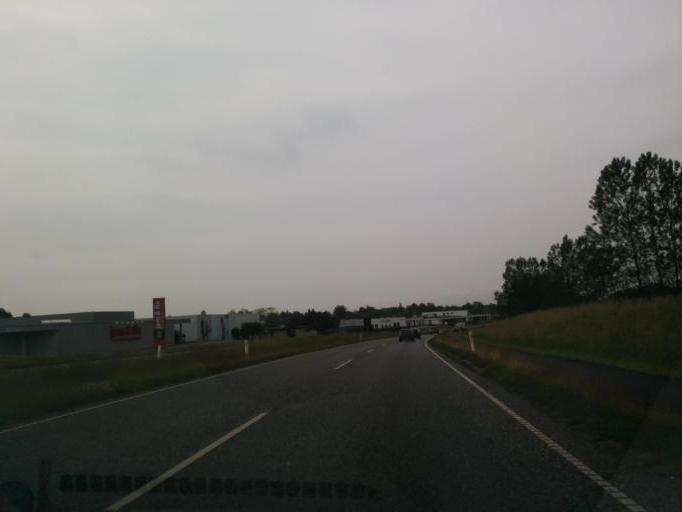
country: DK
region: Central Jutland
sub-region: Arhus Kommune
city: Hjortshoj
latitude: 56.2117
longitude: 10.2775
